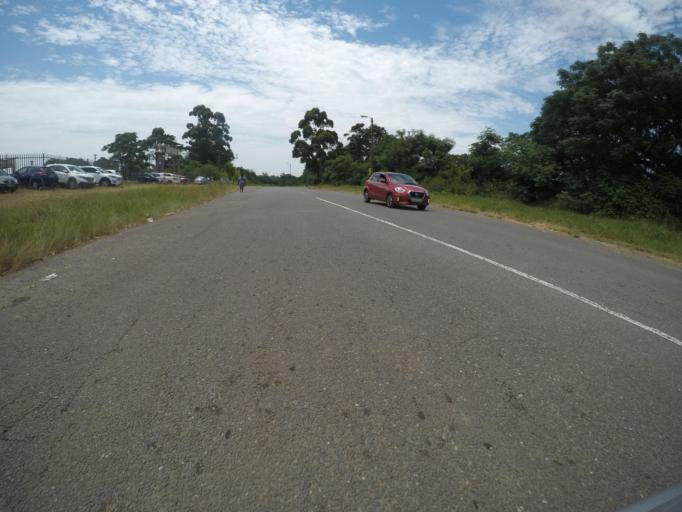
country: ZA
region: Eastern Cape
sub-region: Buffalo City Metropolitan Municipality
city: East London
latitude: -32.9733
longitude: 27.8532
